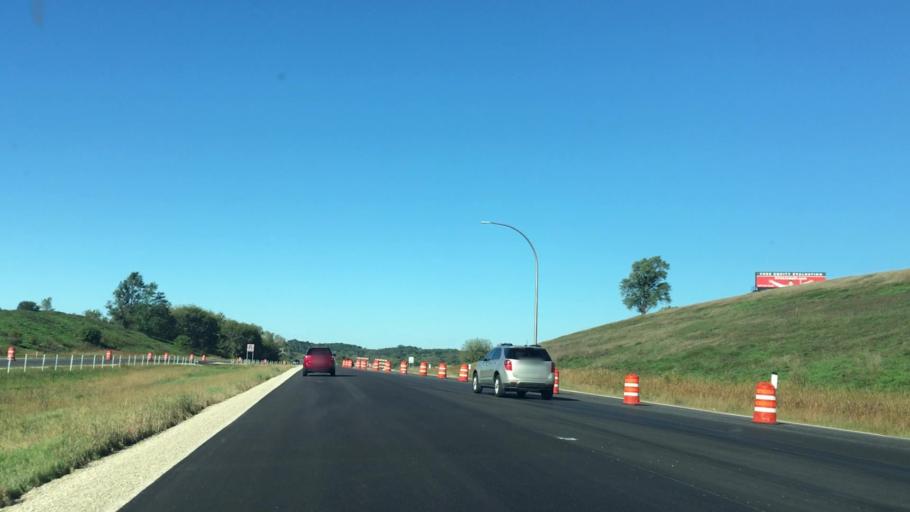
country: US
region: Minnesota
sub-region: Olmsted County
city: Rochester
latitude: 43.9740
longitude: -92.4457
